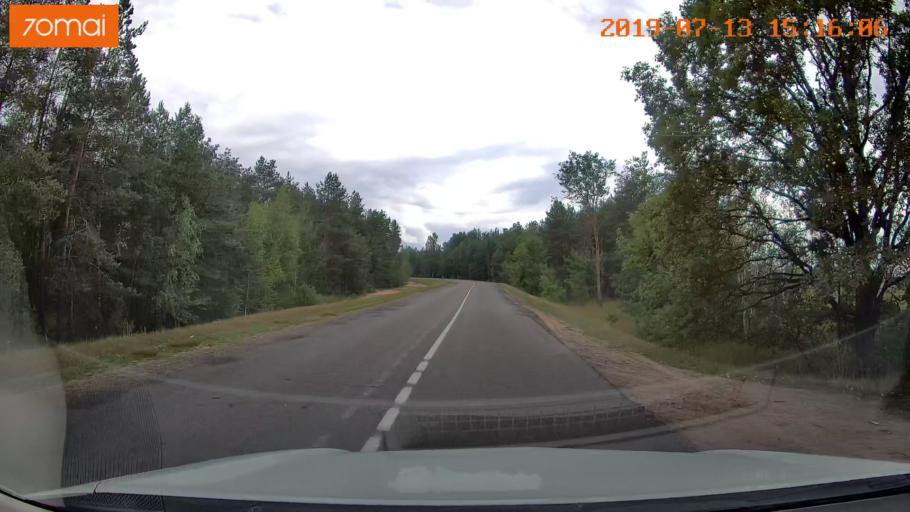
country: BY
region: Mogilev
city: Hlusha
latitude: 53.1107
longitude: 28.8289
